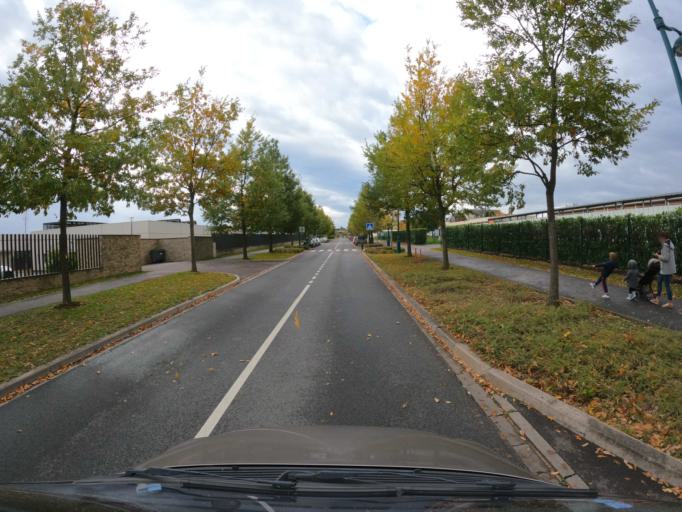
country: FR
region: Ile-de-France
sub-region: Departement de Seine-et-Marne
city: Magny-le-Hongre
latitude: 48.8687
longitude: 2.8118
